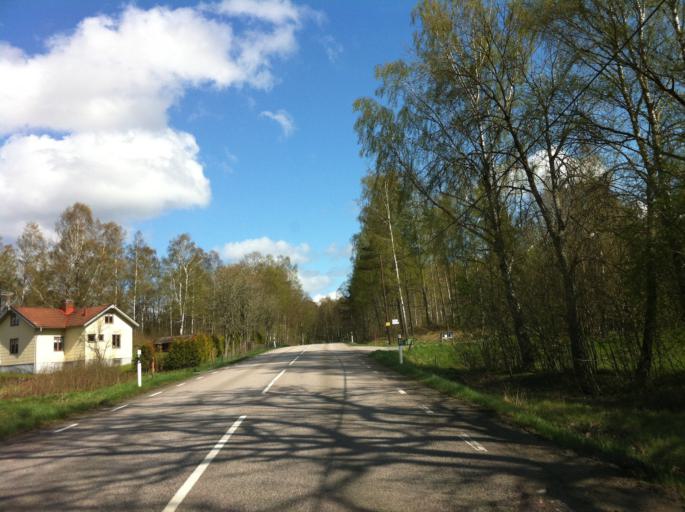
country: SE
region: Vaestra Goetaland
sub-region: Alingsas Kommun
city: Alingsas
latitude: 57.8693
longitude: 12.5747
